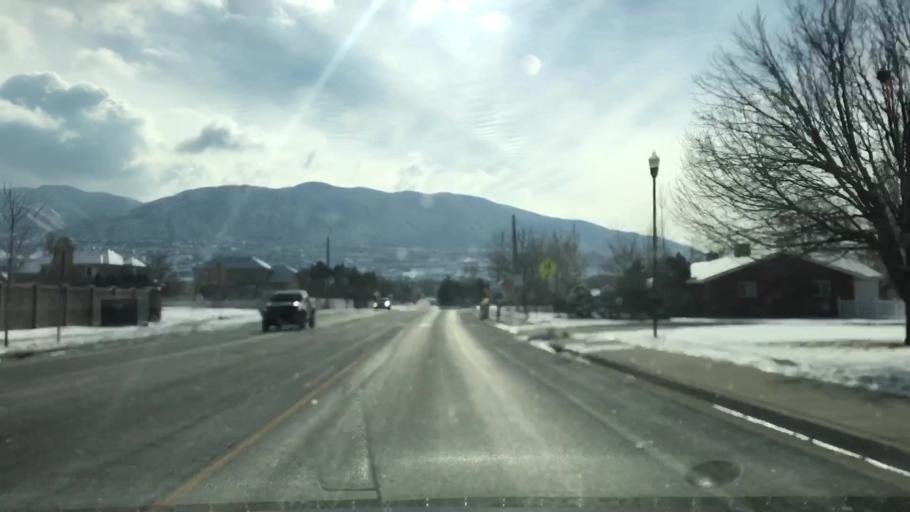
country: US
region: Utah
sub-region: Salt Lake County
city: Draper
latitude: 40.5095
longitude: -111.8818
